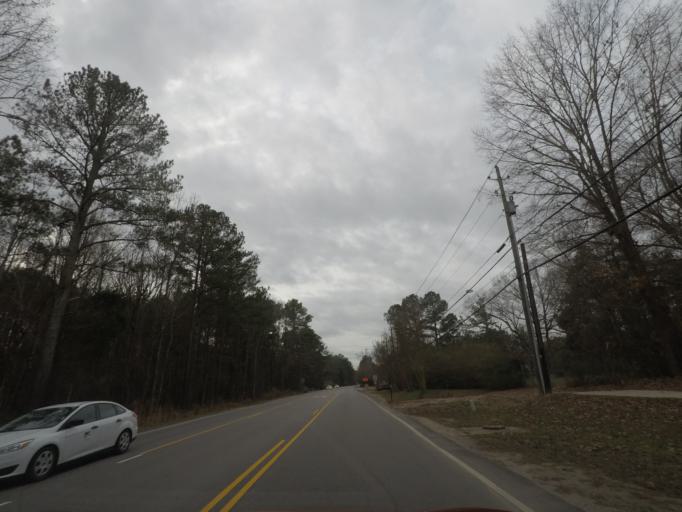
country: US
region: North Carolina
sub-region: Wake County
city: Morrisville
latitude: 35.8283
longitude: -78.8188
